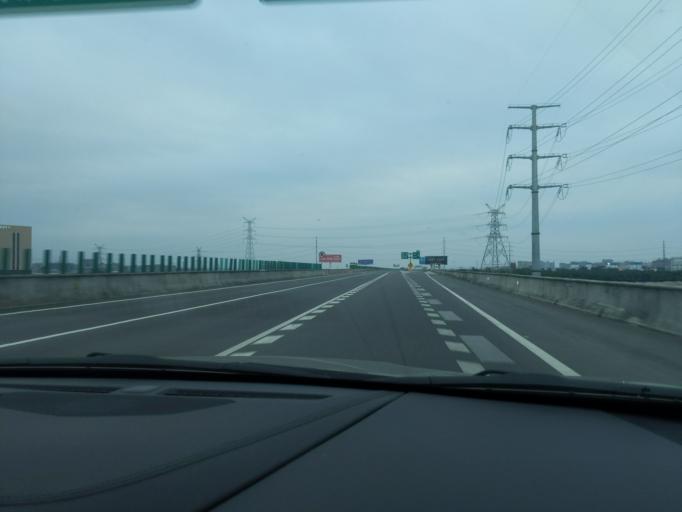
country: CN
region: Fujian
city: Xibin
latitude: 24.7707
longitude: 118.6212
